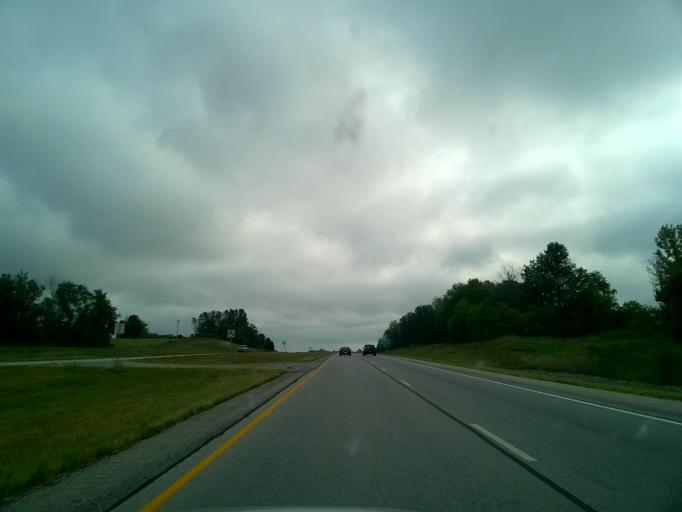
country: US
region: Indiana
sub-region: Floyd County
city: Georgetown
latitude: 38.2623
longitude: -86.0053
